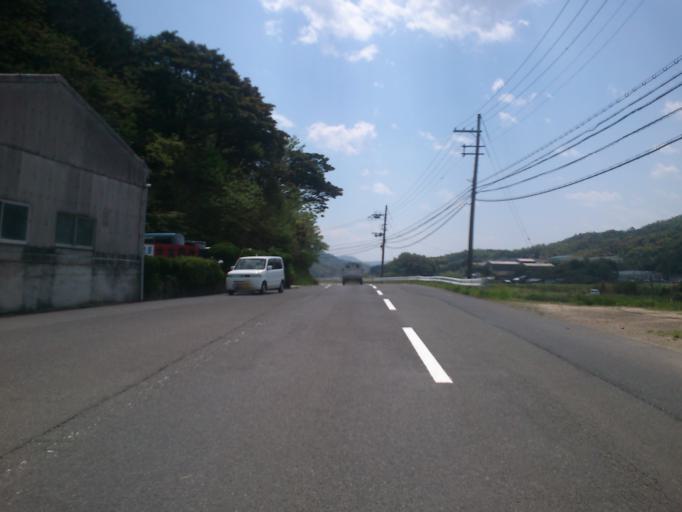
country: JP
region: Kyoto
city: Miyazu
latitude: 35.7272
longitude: 135.1037
